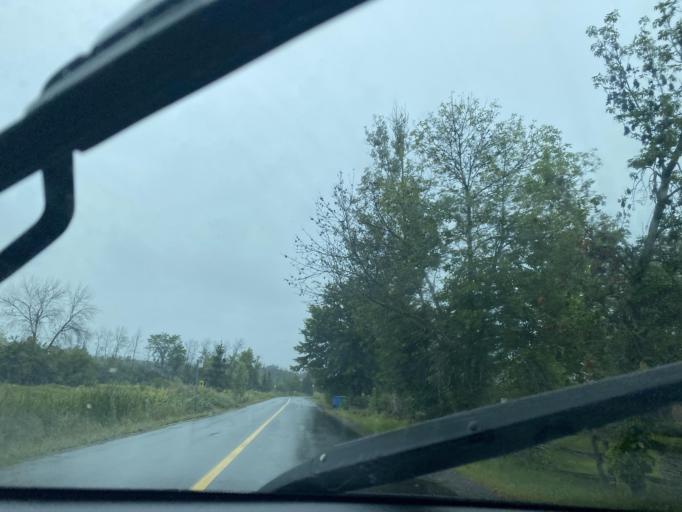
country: CA
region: Quebec
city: Baie-D'Urfe
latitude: 45.4632
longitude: -73.9217
